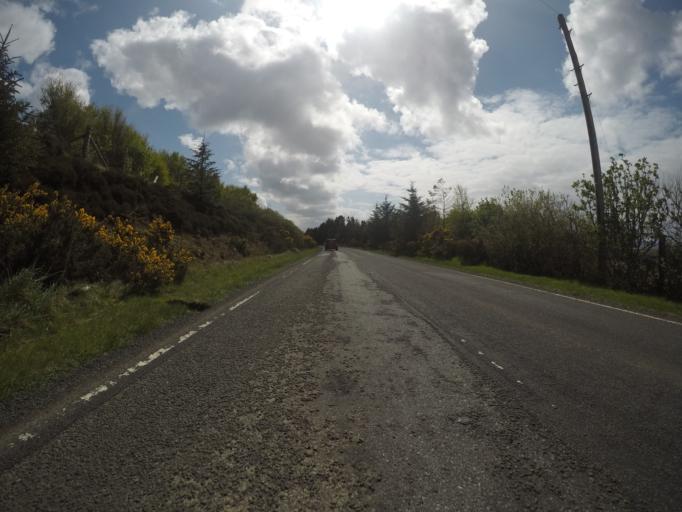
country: GB
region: Scotland
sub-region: Highland
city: Portree
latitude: 57.5710
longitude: -6.3641
